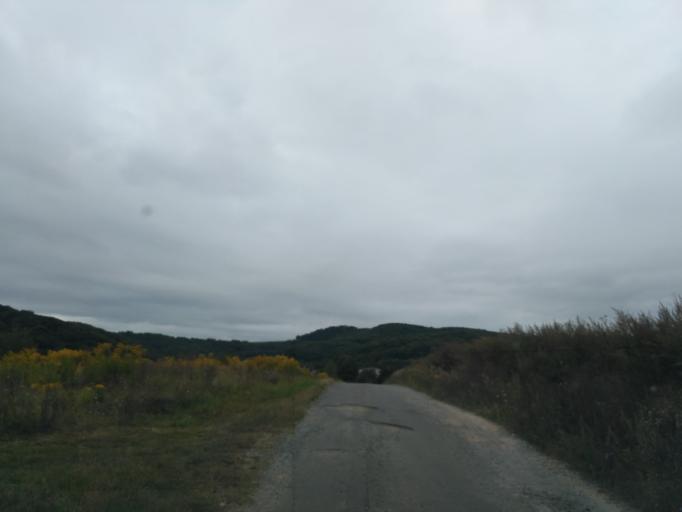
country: SK
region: Presovsky
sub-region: Okres Presov
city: Presov
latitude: 48.9162
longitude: 21.1718
